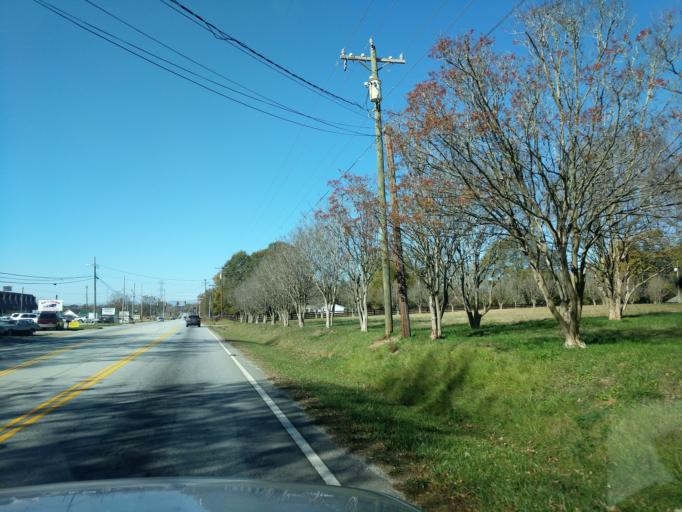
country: US
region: South Carolina
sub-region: Greenville County
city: Taylors
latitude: 34.9552
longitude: -82.2963
